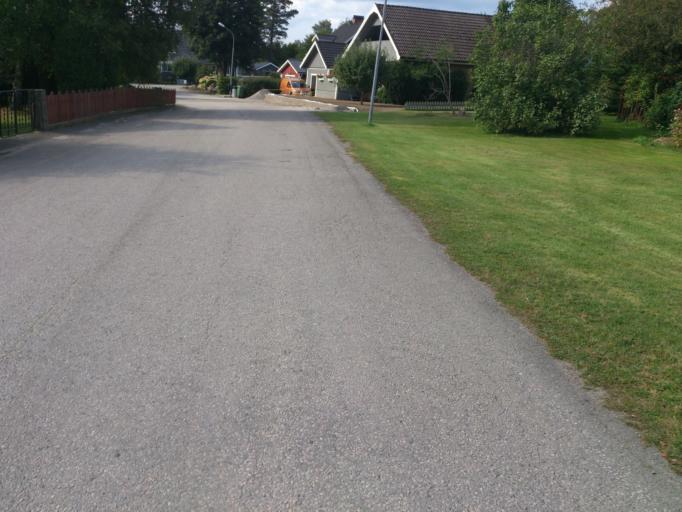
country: SE
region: Kronoberg
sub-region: Alvesta Kommun
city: Moheda
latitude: 56.9933
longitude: 14.5851
